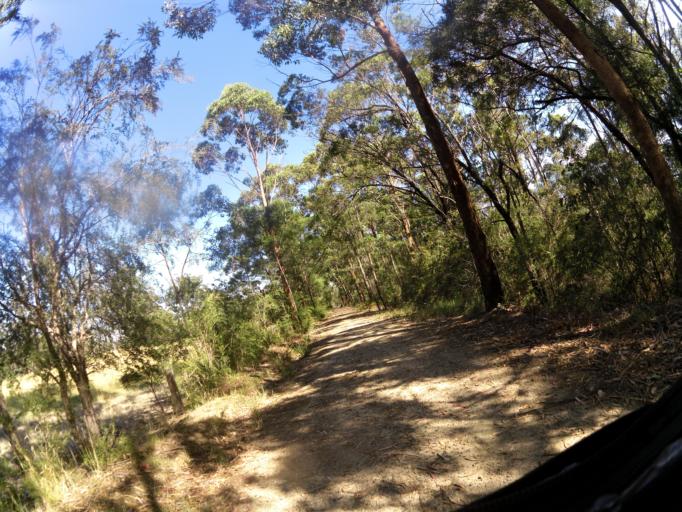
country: AU
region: Victoria
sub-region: East Gippsland
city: Lakes Entrance
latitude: -37.7489
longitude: 148.1801
